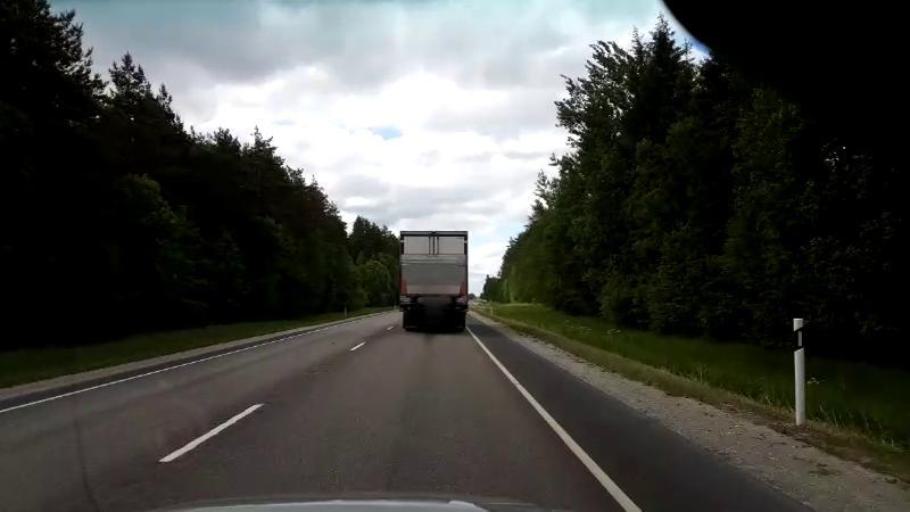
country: EE
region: Raplamaa
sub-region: Maerjamaa vald
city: Marjamaa
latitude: 58.7540
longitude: 24.4233
